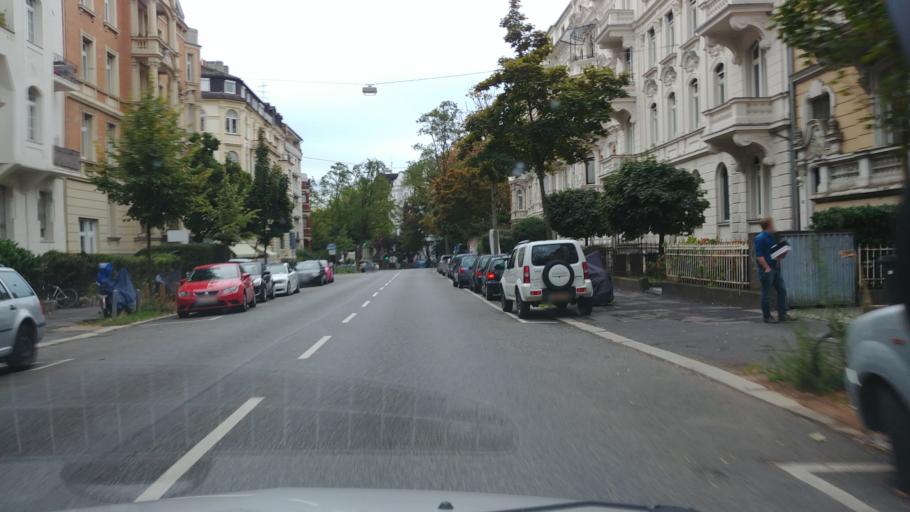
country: DE
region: Hesse
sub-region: Regierungsbezirk Darmstadt
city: Wiesbaden
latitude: 50.0847
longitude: 8.2262
